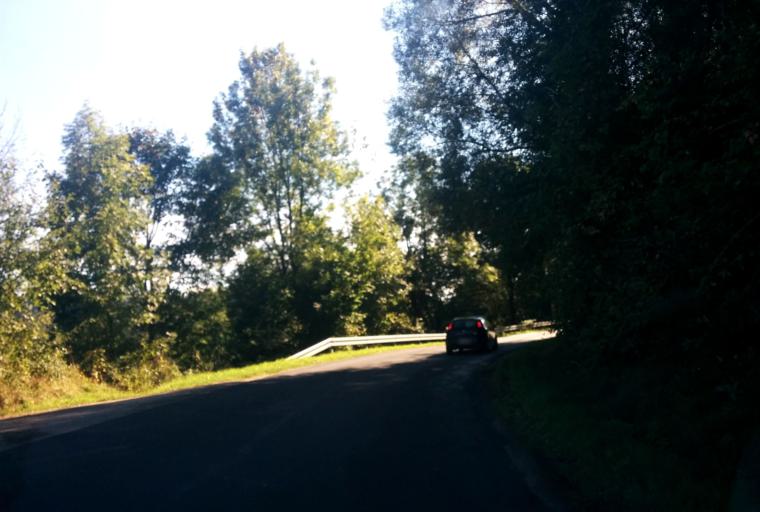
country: PL
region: Subcarpathian Voivodeship
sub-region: Powiat leski
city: Polanczyk
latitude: 49.3294
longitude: 22.4194
